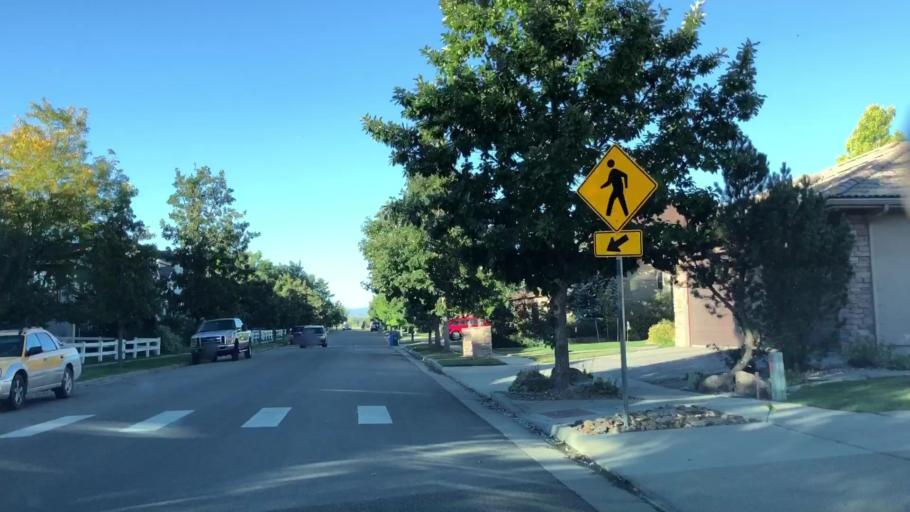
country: US
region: Colorado
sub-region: Larimer County
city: Loveland
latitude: 40.4420
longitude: -105.0259
